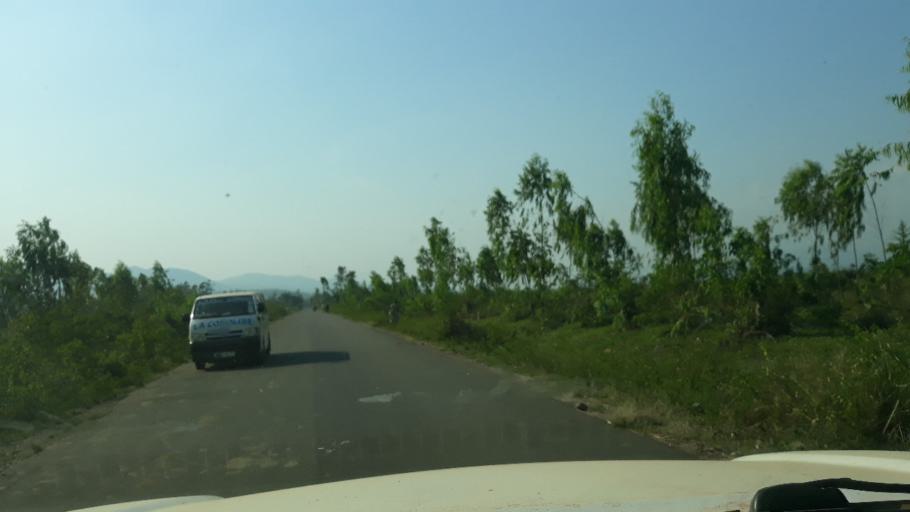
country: BI
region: Cibitoke
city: Cibitoke
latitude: -2.8013
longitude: 29.0007
